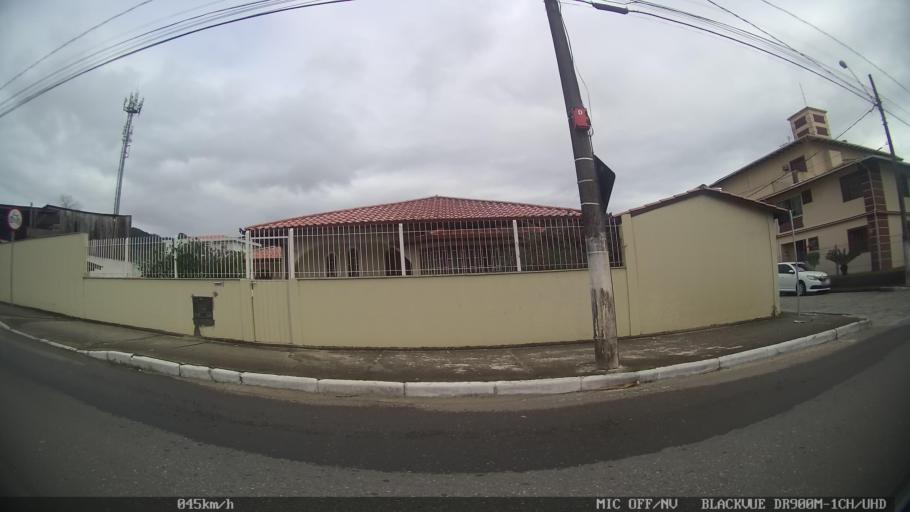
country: BR
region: Santa Catarina
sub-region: Sao Jose
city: Campinas
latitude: -27.5686
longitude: -48.6313
